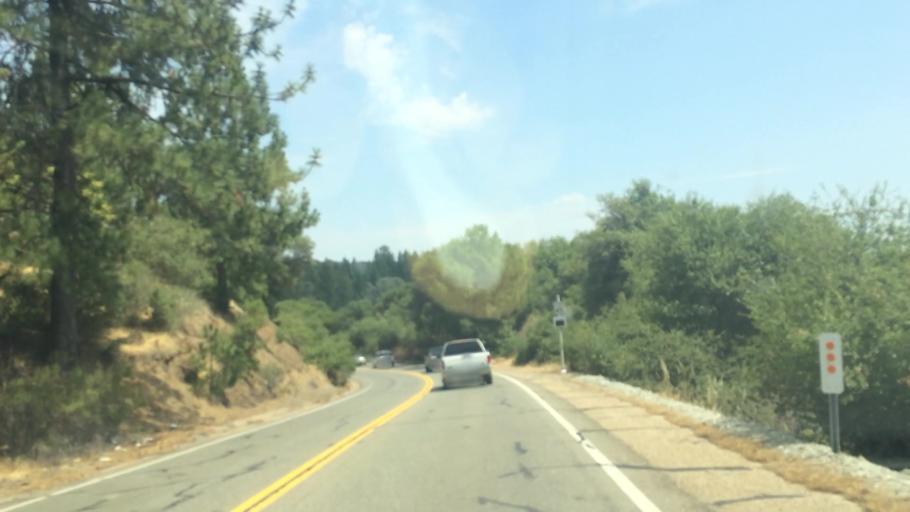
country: US
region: California
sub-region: Amador County
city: Jackson
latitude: 38.3986
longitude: -120.7433
